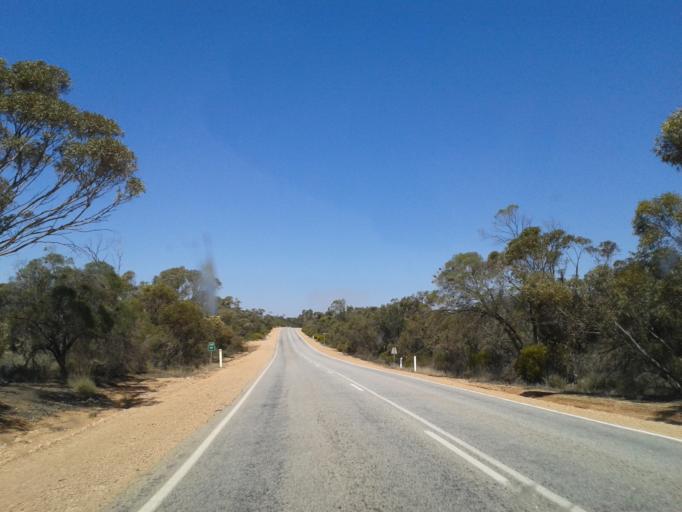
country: AU
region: Victoria
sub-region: Swan Hill
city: Swan Hill
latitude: -34.7384
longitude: 143.1804
